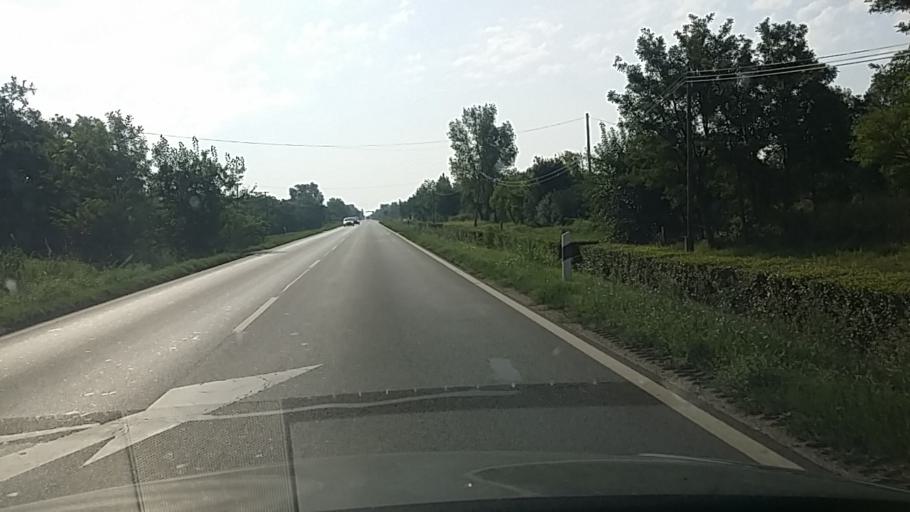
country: HU
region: Bekes
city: Kondoros
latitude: 46.8024
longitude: 20.7090
